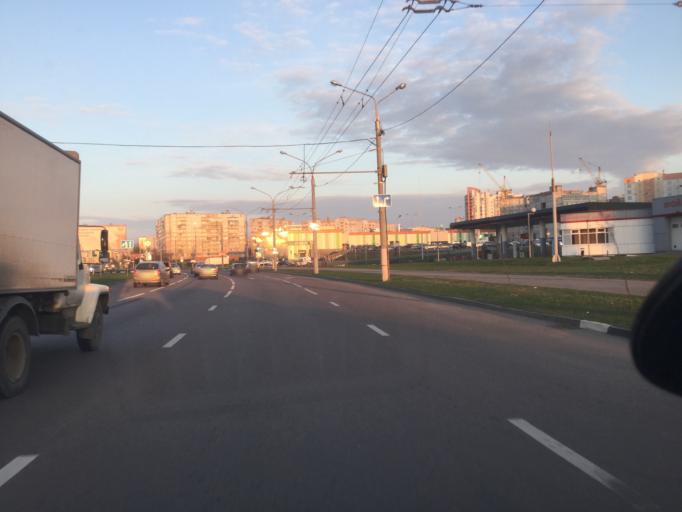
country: BY
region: Vitebsk
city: Vitebsk
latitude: 55.1643
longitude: 30.2038
